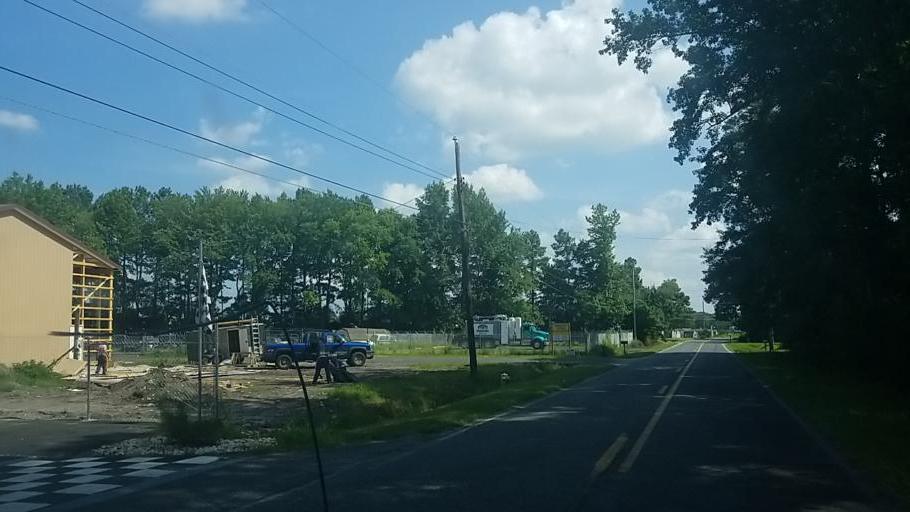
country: US
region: Maryland
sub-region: Wicomico County
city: Fruitland
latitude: 38.3101
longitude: -75.6320
